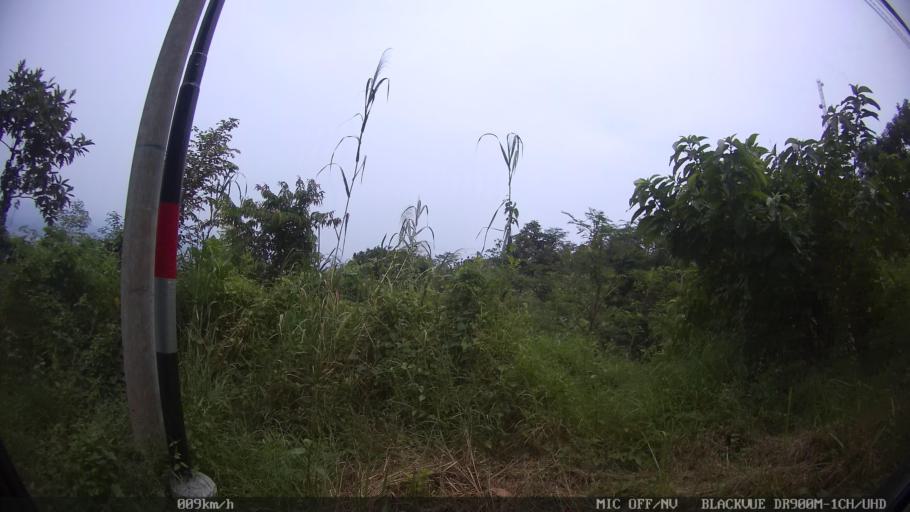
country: ID
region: Lampung
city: Panjang
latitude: -5.4324
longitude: 105.3087
